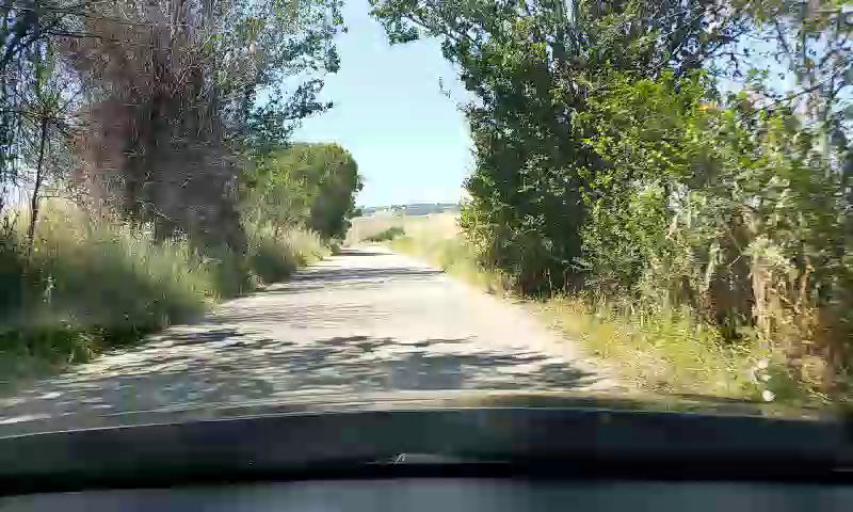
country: IT
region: Molise
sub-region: Provincia di Campobasso
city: Montecilfone
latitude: 41.9284
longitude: 14.8551
